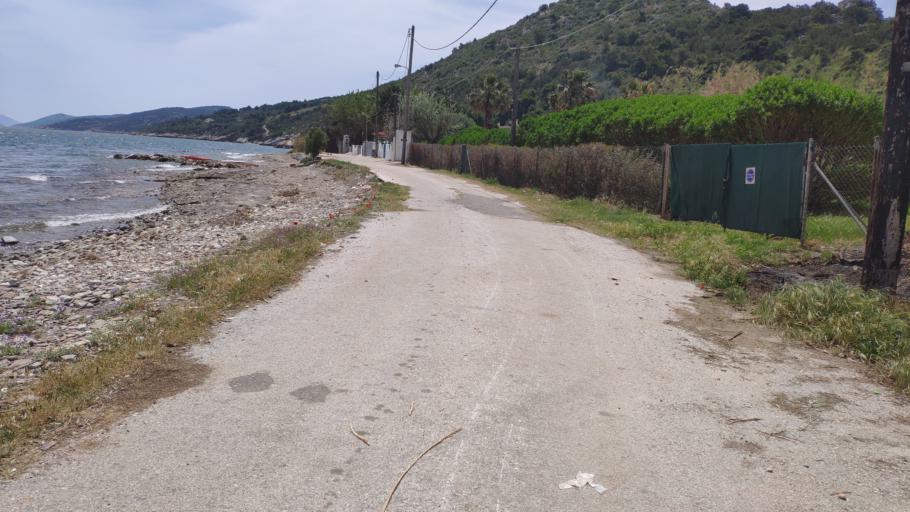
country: GR
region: Attica
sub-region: Nomarchia Anatolikis Attikis
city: Grammatiko
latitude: 38.2615
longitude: 23.9820
